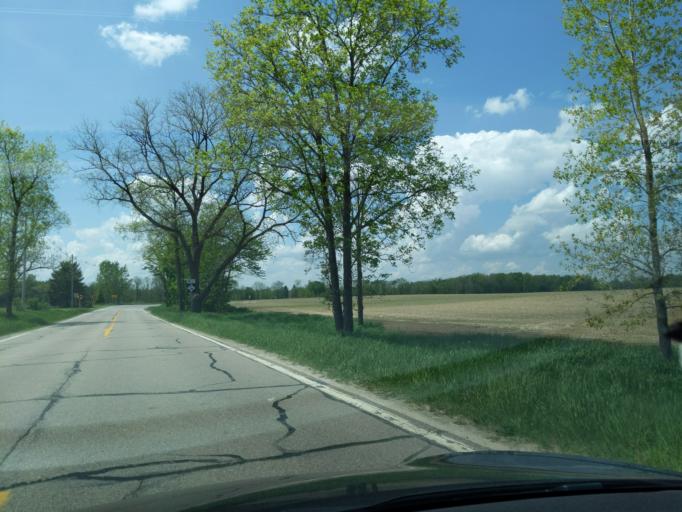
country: US
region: Michigan
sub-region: Ingham County
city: Stockbridge
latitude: 42.4968
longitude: -84.1194
